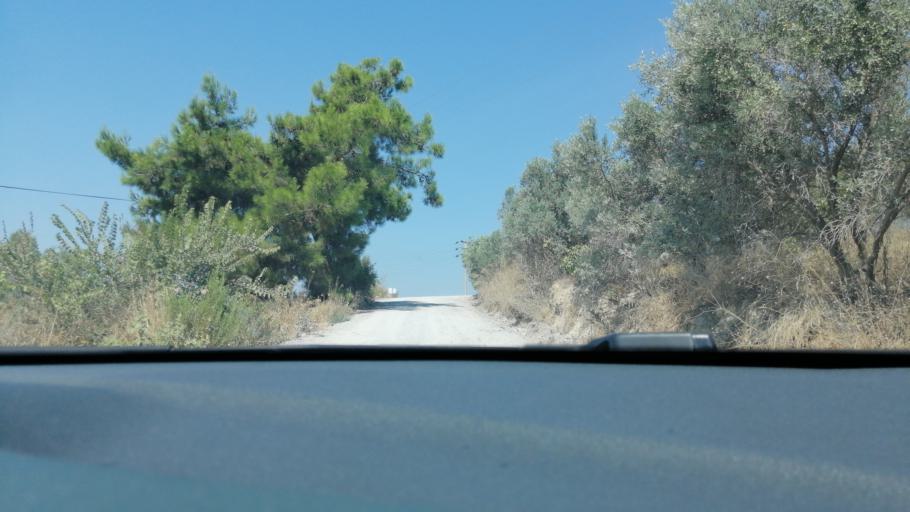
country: TR
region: Aydin
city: Davutlar
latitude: 37.7857
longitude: 27.3153
